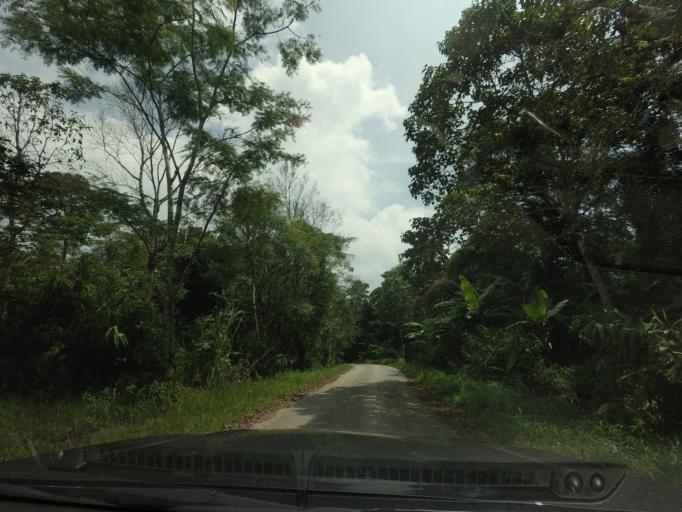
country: TH
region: Loei
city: Phu Ruea
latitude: 17.5026
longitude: 101.3500
